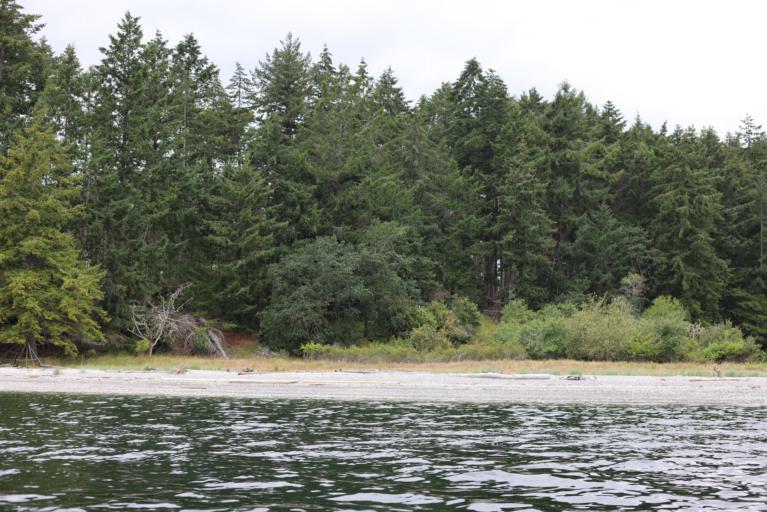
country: CA
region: British Columbia
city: North Cowichan
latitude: 48.9070
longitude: -123.6692
